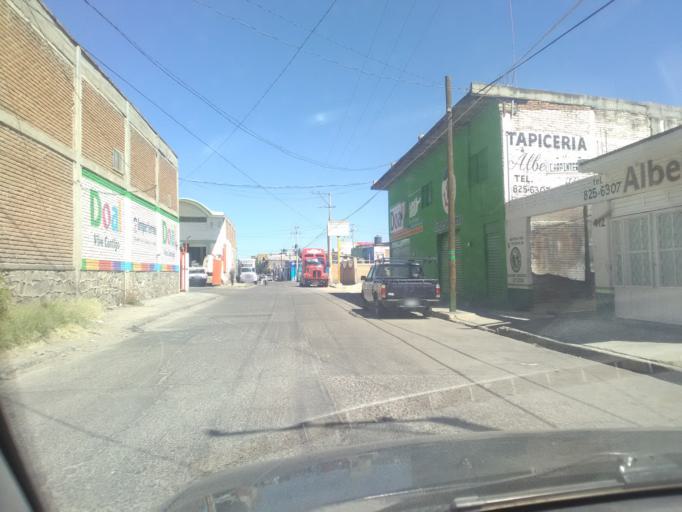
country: MX
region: Durango
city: Victoria de Durango
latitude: 24.0153
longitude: -104.6593
